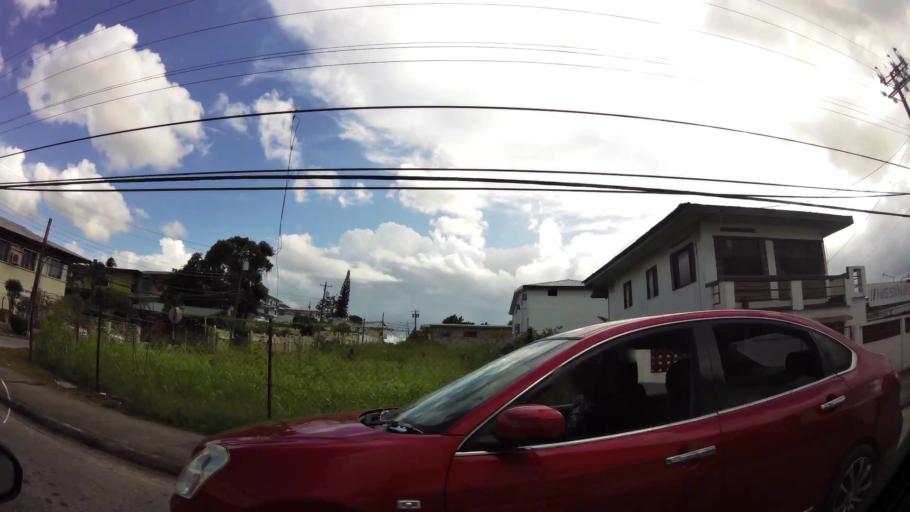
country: TT
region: City of San Fernando
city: Mon Repos
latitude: 10.2681
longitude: -61.4571
